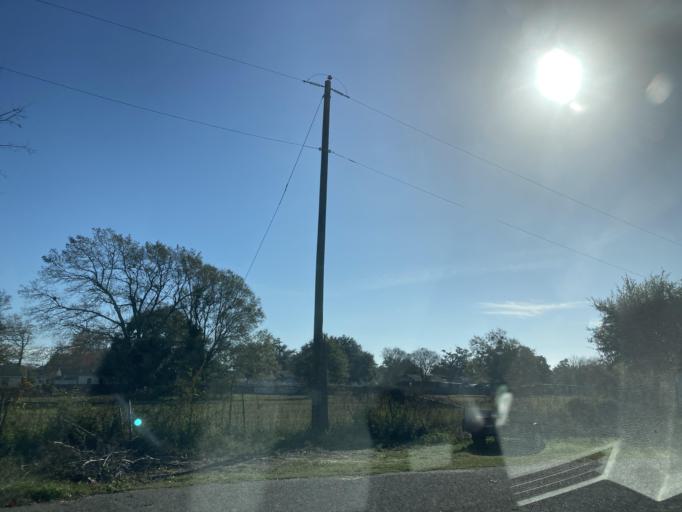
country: US
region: Mississippi
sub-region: Harrison County
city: Biloxi
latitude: 30.3975
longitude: -88.9429
